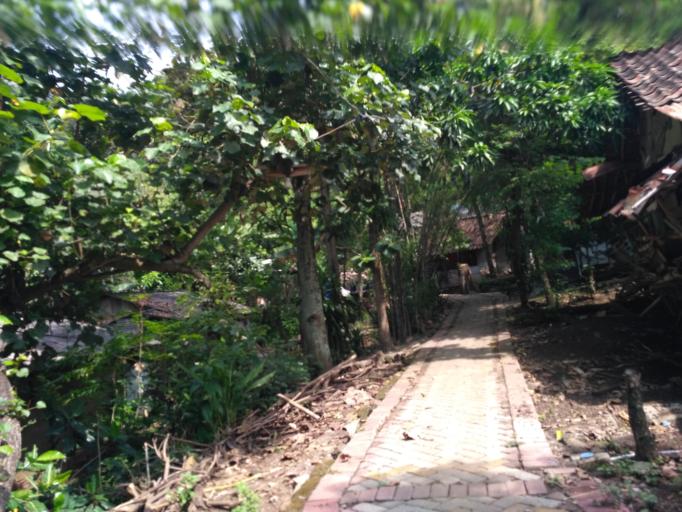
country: ID
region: Central Java
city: Semarang
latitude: -7.0449
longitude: 110.4426
